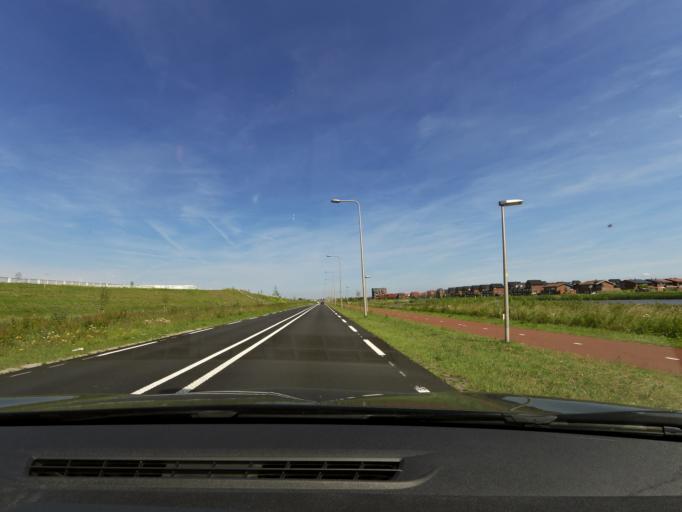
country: NL
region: South Holland
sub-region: Gemeente Binnenmaas
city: Heinenoord
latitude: 51.8604
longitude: 4.4616
